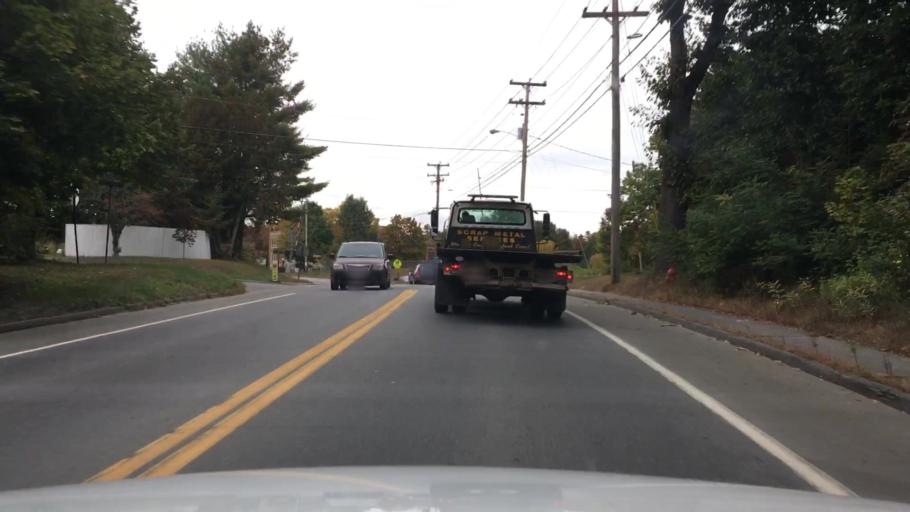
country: US
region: Maine
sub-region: Kennebec County
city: Oakland
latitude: 44.5493
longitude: -69.7152
